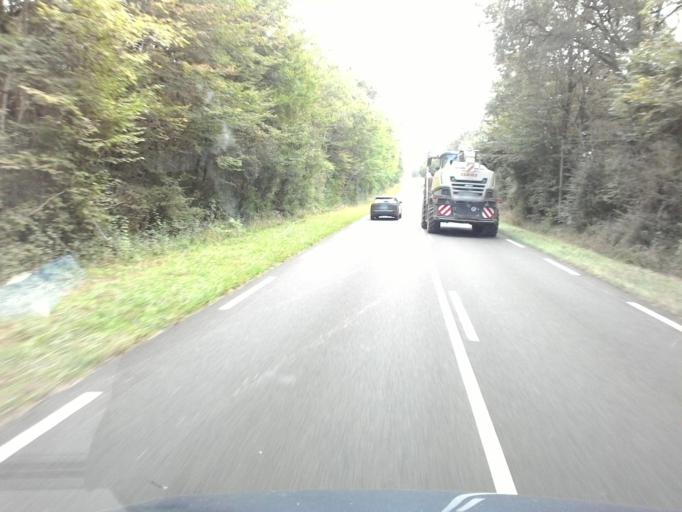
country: FR
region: Bourgogne
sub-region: Departement de Saone-et-Loire
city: Saint-Gengoux-le-National
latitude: 46.5716
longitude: 4.5437
